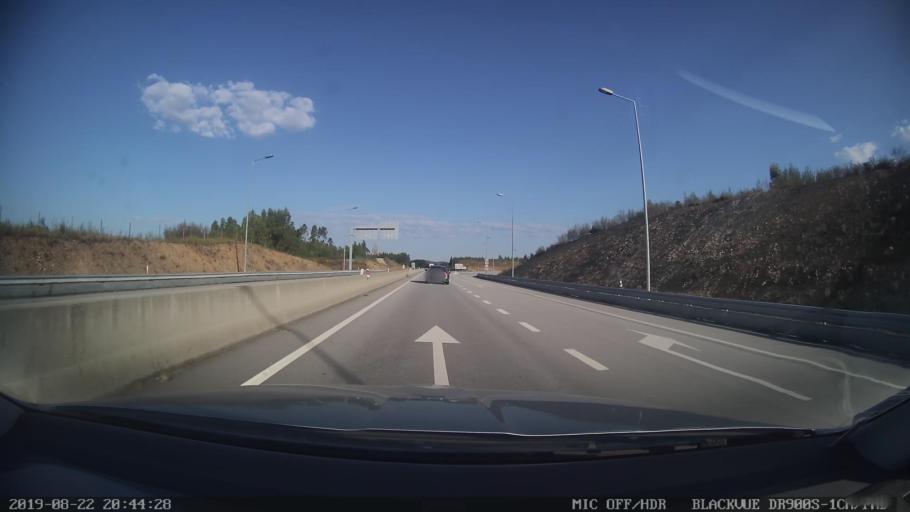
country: PT
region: Castelo Branco
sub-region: Proenca-A-Nova
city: Proenca-a-Nova
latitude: 39.7076
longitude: -7.8519
